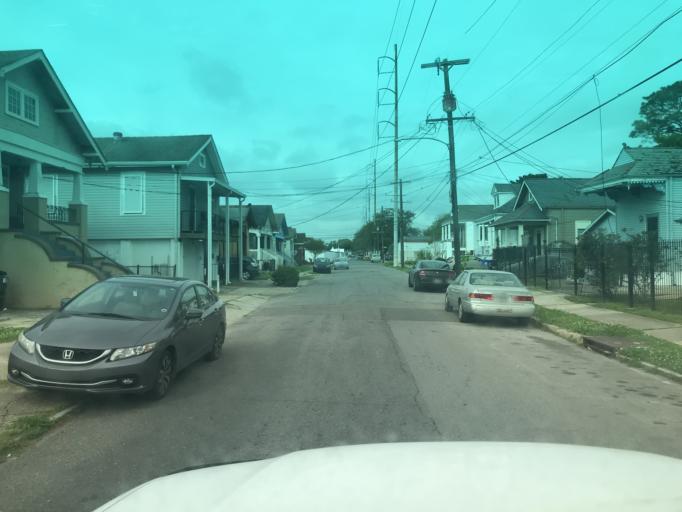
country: US
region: Louisiana
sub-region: Orleans Parish
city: New Orleans
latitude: 29.9761
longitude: -90.0493
